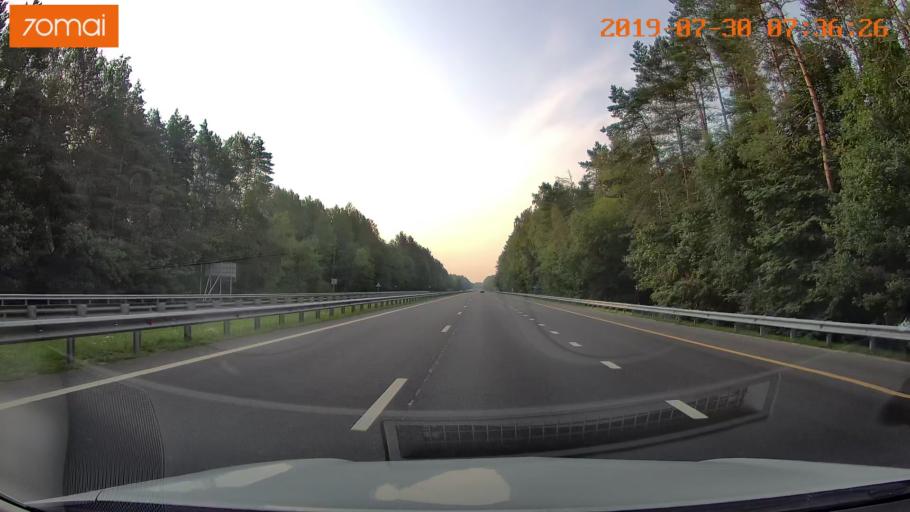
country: RU
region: Kaliningrad
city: Gvardeysk
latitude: 54.6645
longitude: 21.1244
